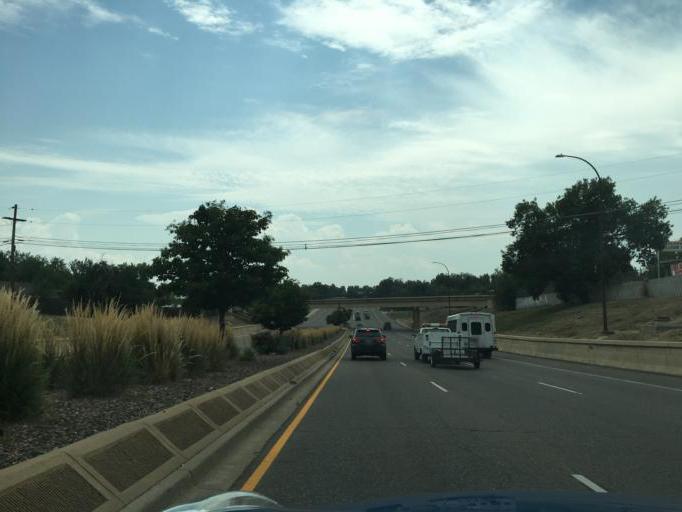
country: US
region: Colorado
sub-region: Jefferson County
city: Arvada
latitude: 39.8081
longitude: -105.0785
